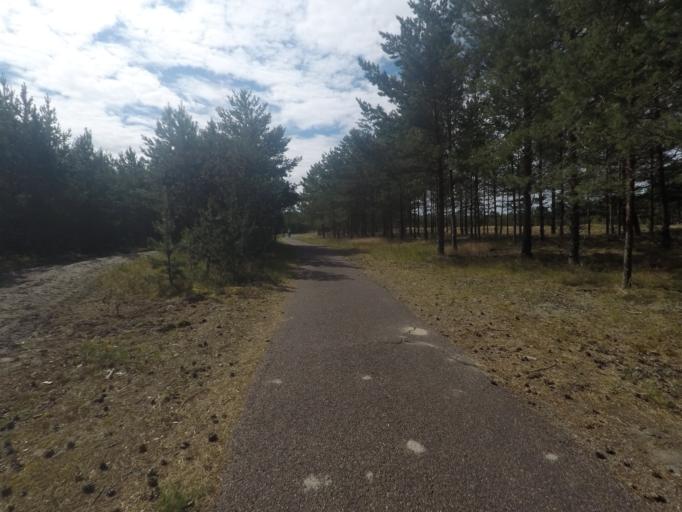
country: LT
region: Klaipedos apskritis
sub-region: Klaipeda
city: Klaipeda
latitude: 55.5748
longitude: 21.1136
